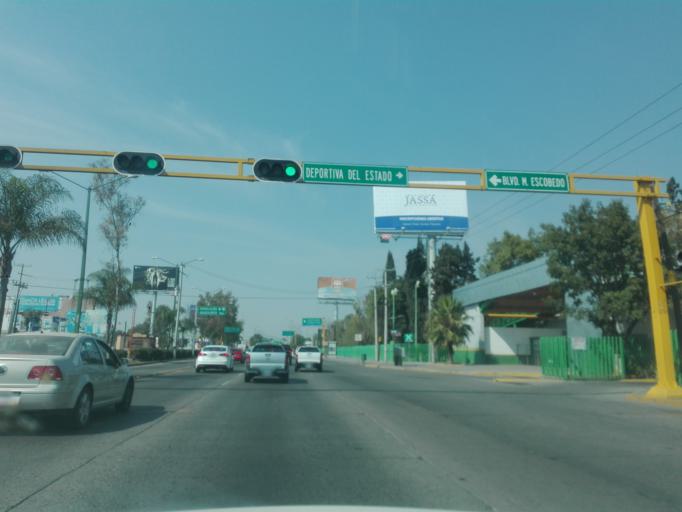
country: MX
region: Guanajuato
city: Leon
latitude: 21.1041
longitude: -101.6379
